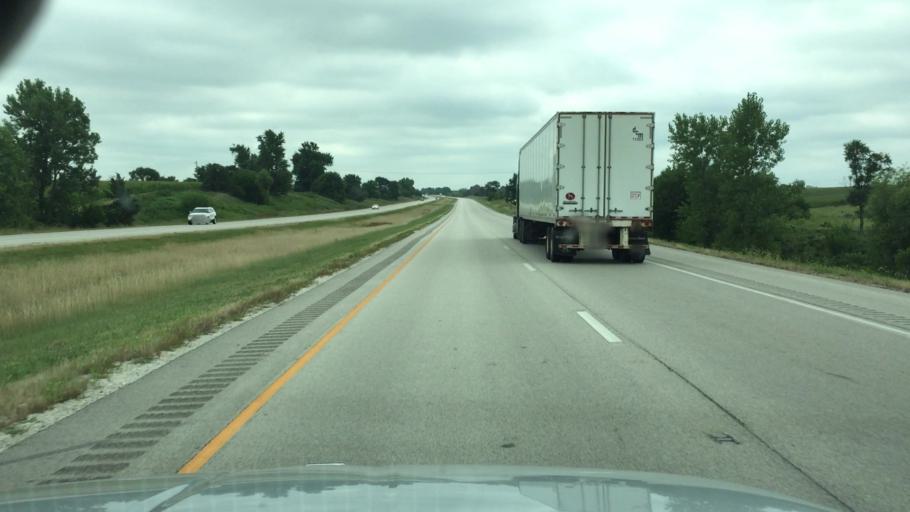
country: US
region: Illinois
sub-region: Henry County
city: Orion
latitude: 41.3419
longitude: -90.3333
